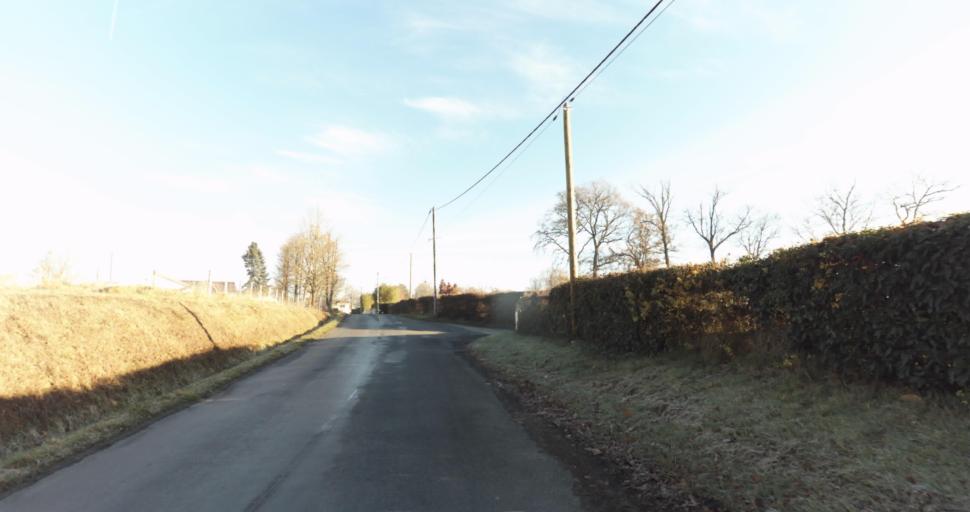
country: FR
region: Limousin
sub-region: Departement de la Haute-Vienne
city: Aixe-sur-Vienne
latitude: 45.8146
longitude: 1.1508
